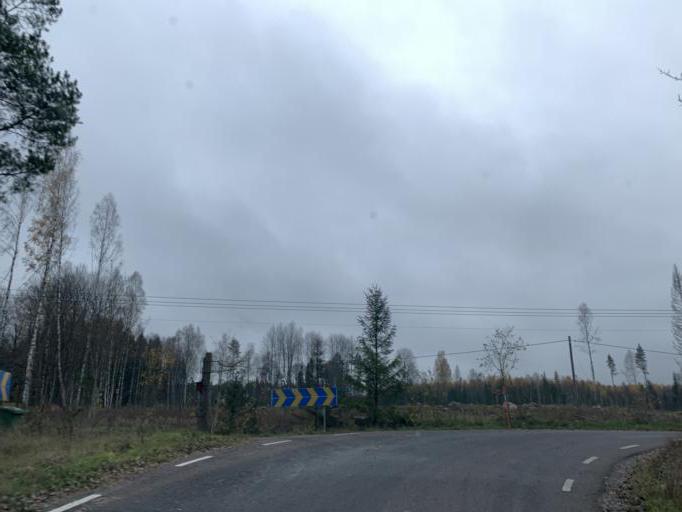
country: SE
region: Vaestmanland
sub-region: Surahammars Kommun
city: Surahammar
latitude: 59.6759
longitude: 16.0819
